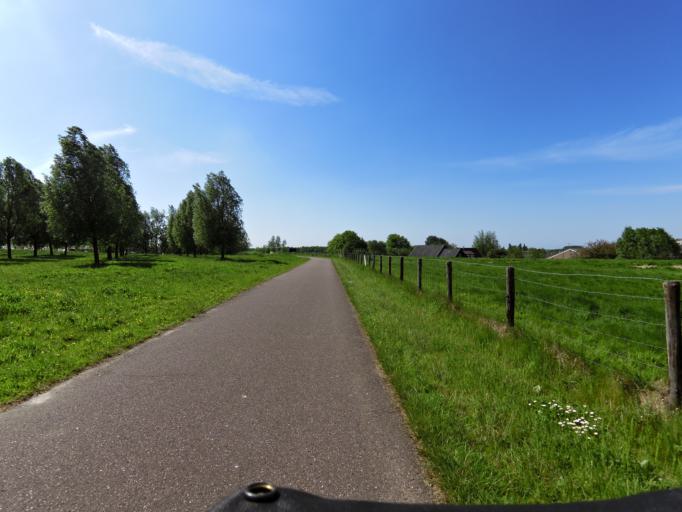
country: NL
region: South Holland
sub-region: Gemeente Binnenmaas
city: Heinenoord
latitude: 51.8405
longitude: 4.4966
